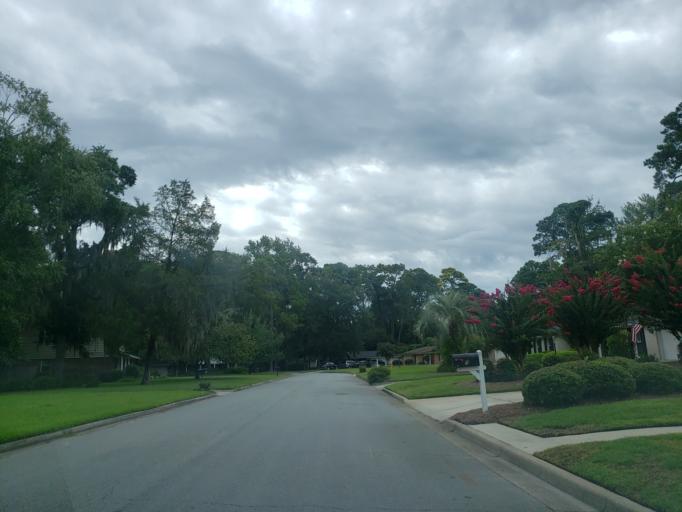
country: US
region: Georgia
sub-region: Chatham County
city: Isle of Hope
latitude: 31.9919
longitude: -81.0541
